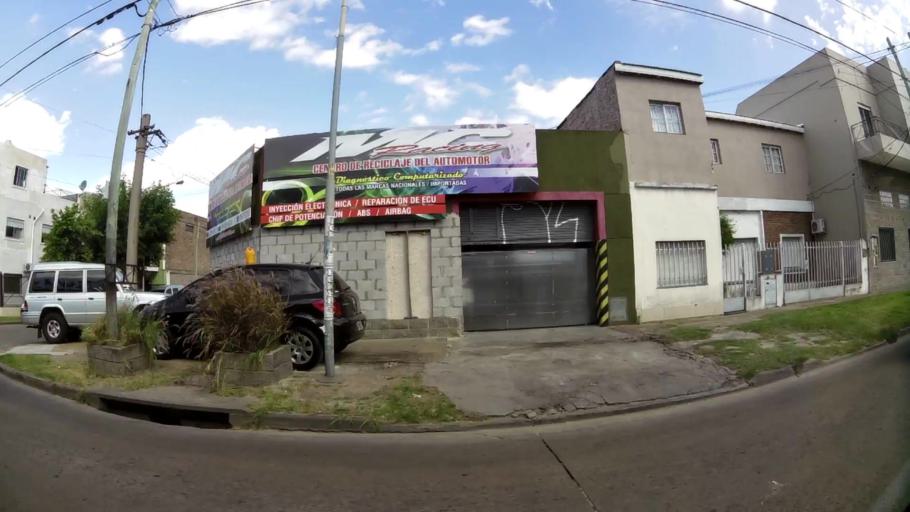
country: AR
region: Buenos Aires
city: San Justo
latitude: -34.6574
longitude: -58.5810
